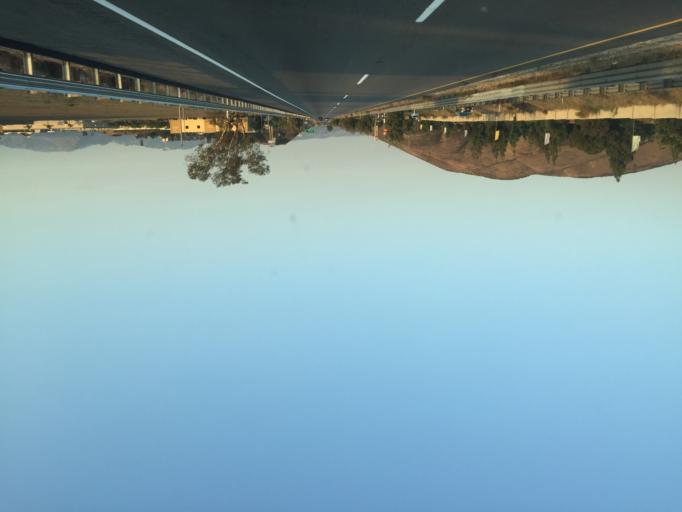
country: US
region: California
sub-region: San Bernardino County
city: Muscoy
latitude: 34.1703
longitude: -117.3384
